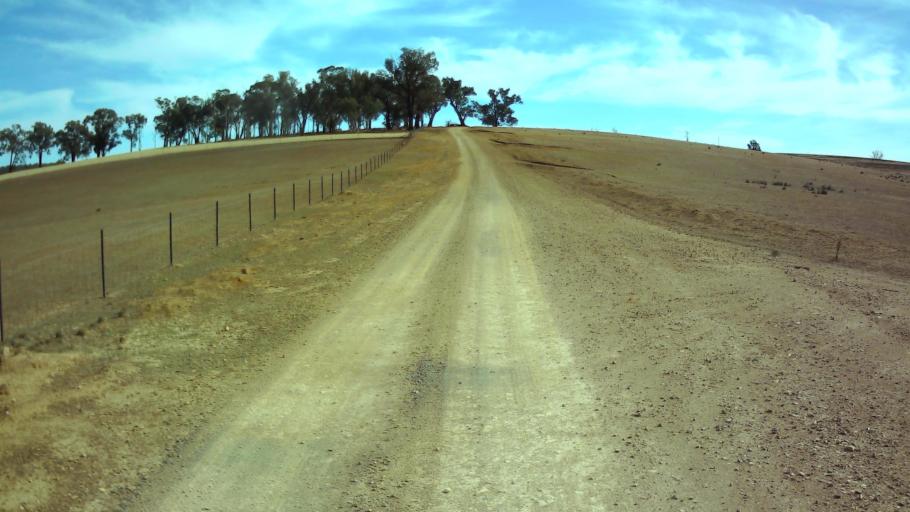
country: AU
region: New South Wales
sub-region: Weddin
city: Grenfell
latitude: -33.8962
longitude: 148.2038
